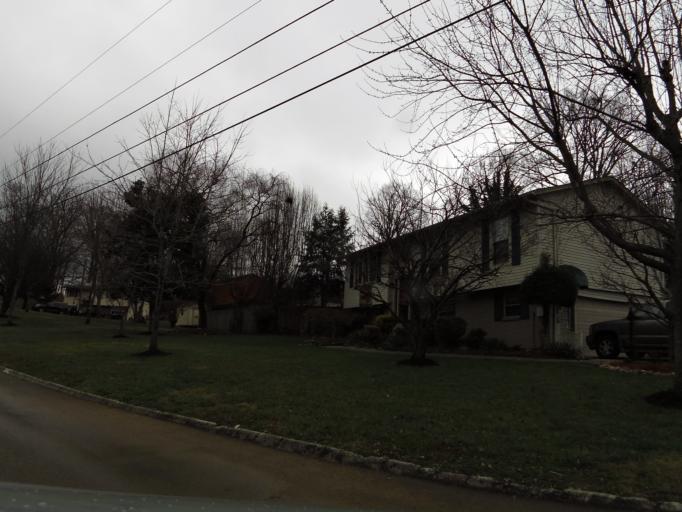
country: US
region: Tennessee
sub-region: Knox County
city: Knoxville
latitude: 35.9912
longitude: -84.0223
